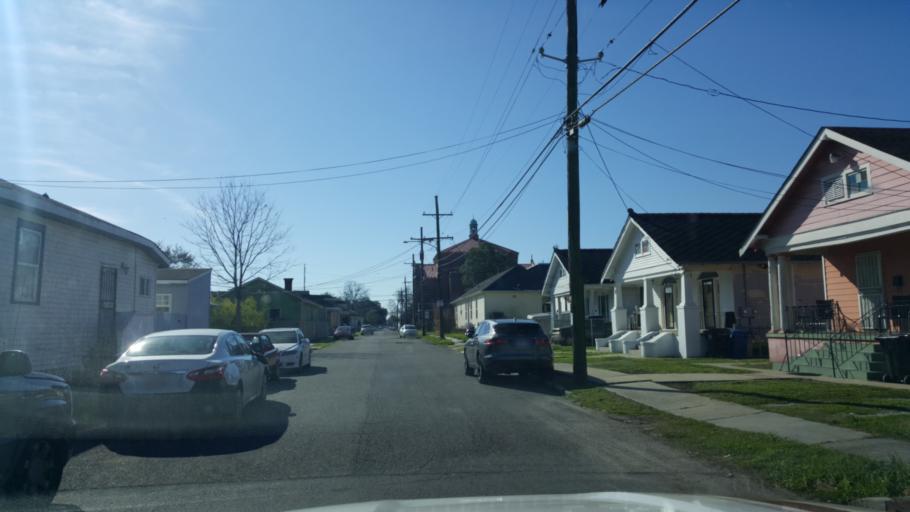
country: US
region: Louisiana
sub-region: Orleans Parish
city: New Orleans
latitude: 29.9790
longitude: -90.0518
